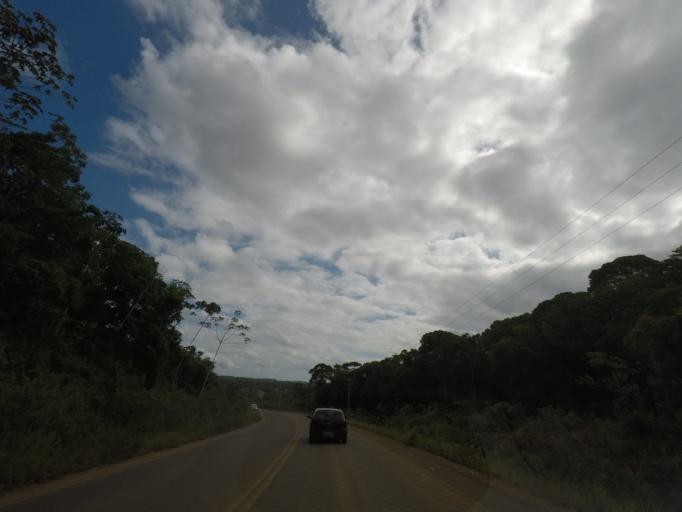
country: BR
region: Bahia
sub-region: Itacare
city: Itacare
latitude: -14.2063
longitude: -39.1009
